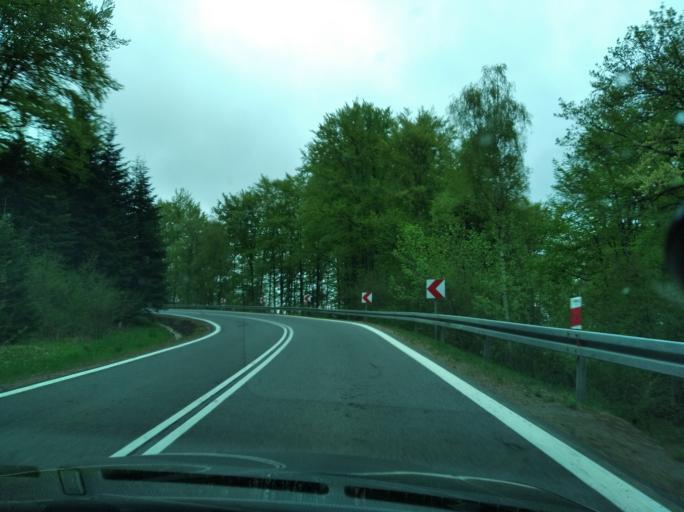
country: PL
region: Subcarpathian Voivodeship
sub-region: Powiat sanocki
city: Tyrawa Woloska
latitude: 49.5577
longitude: 22.3363
